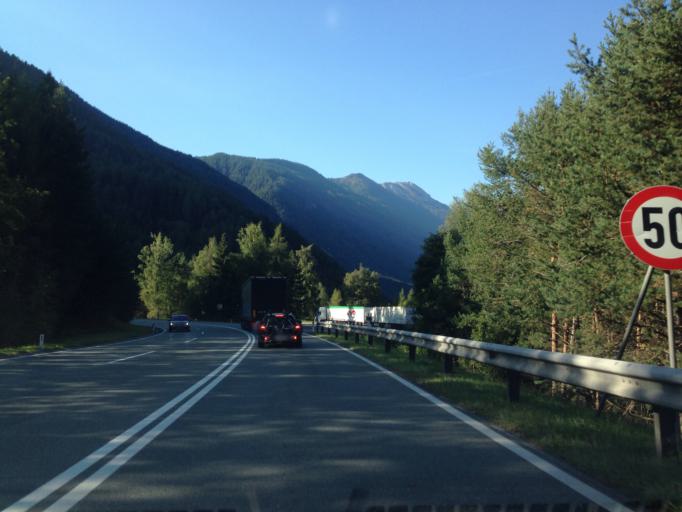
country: AT
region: Tyrol
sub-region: Politischer Bezirk Imst
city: Nassereith
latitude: 47.3035
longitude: 10.8583
